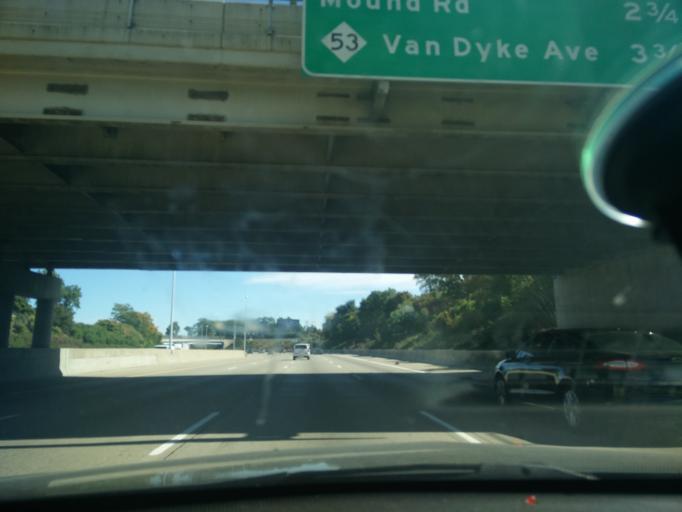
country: US
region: Michigan
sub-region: Oakland County
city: Madison Heights
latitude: 42.4770
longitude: -83.0948
